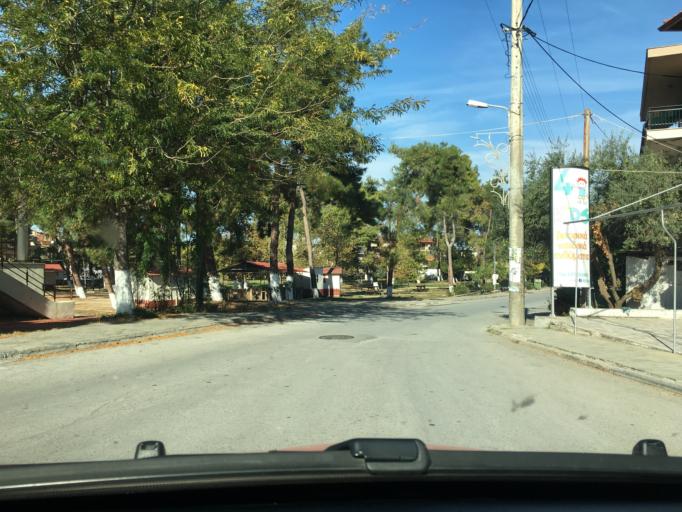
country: GR
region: Central Macedonia
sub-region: Nomos Chalkidikis
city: Ierissos
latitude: 40.3970
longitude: 23.8774
